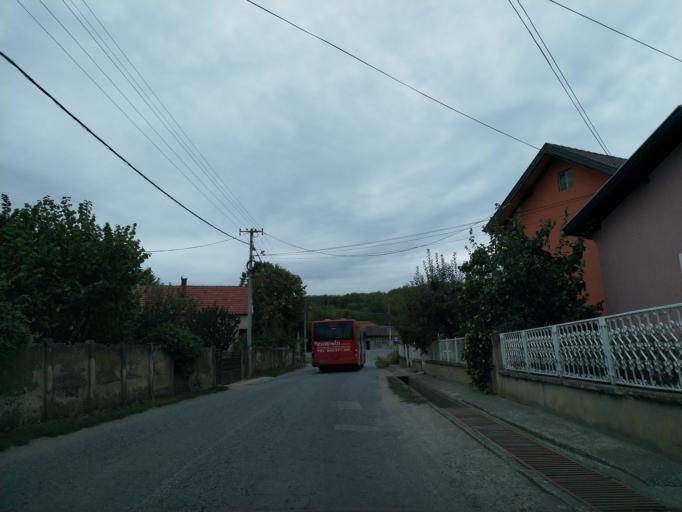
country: RS
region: Central Serbia
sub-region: Pomoravski Okrug
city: Paracin
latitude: 43.8354
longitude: 21.3228
